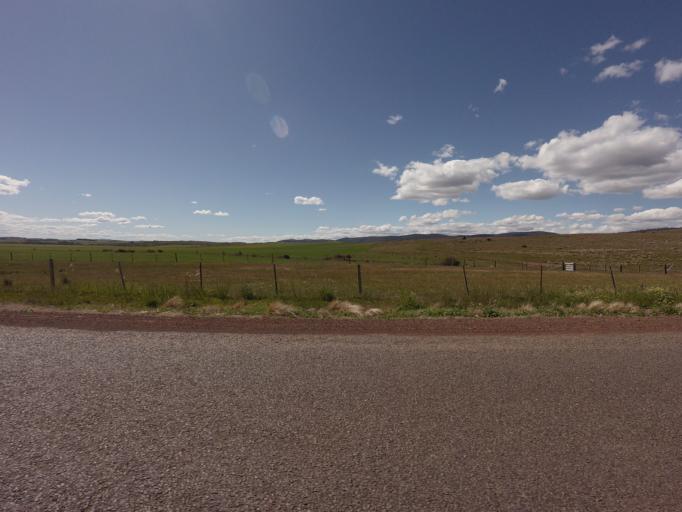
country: AU
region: Tasmania
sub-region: Northern Midlands
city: Evandale
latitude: -41.9399
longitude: 147.5577
